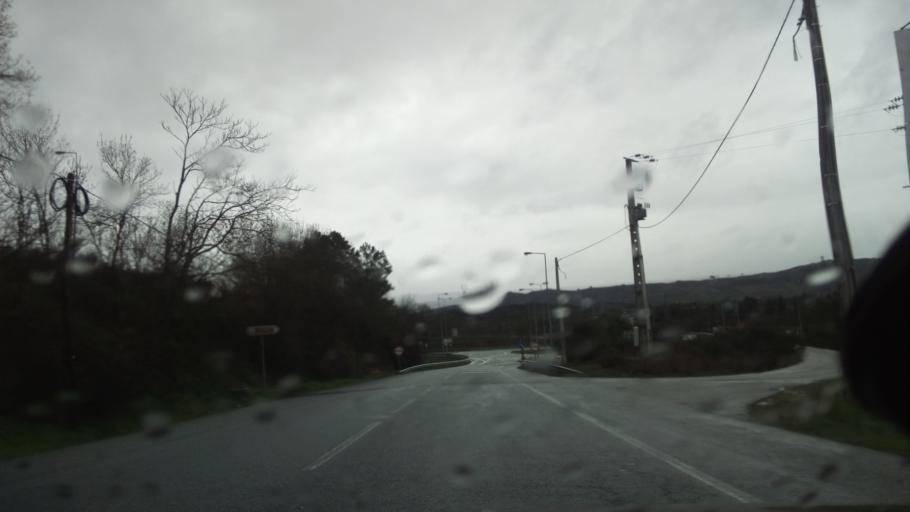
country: PT
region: Guarda
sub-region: Celorico da Beira
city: Celorico da Beira
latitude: 40.6297
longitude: -7.4111
